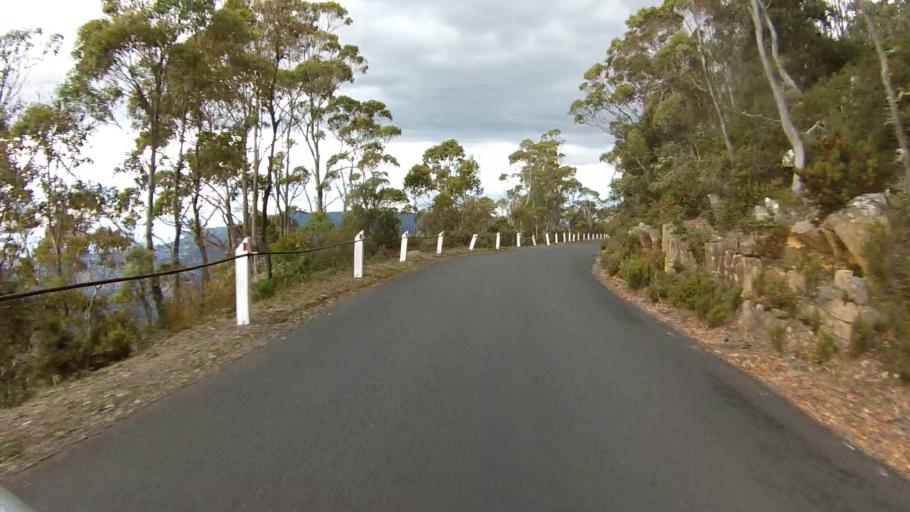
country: AU
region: Tasmania
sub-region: Glenorchy
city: West Moonah
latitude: -42.8912
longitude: 147.2429
